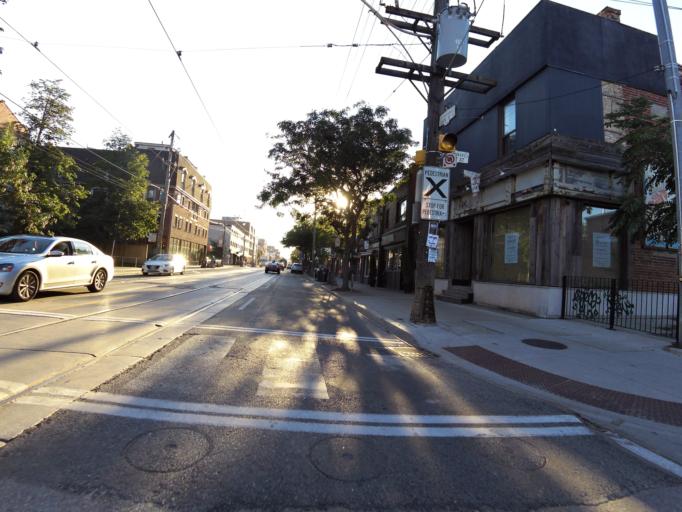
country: CA
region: Ontario
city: Toronto
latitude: 43.6630
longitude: -79.3314
